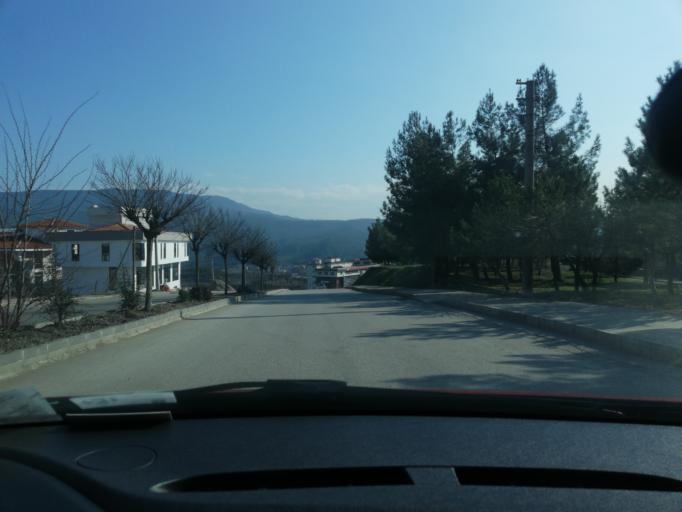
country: TR
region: Karabuk
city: Safranbolu
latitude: 41.2311
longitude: 32.6688
